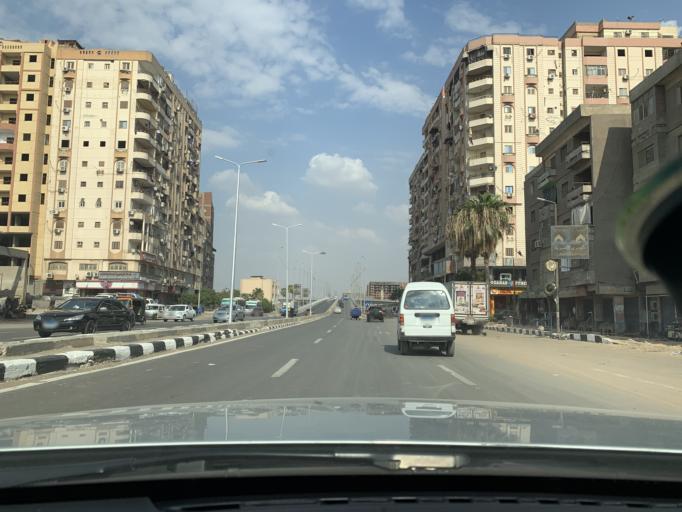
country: EG
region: Muhafazat al Qahirah
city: Cairo
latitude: 30.1316
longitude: 31.2854
